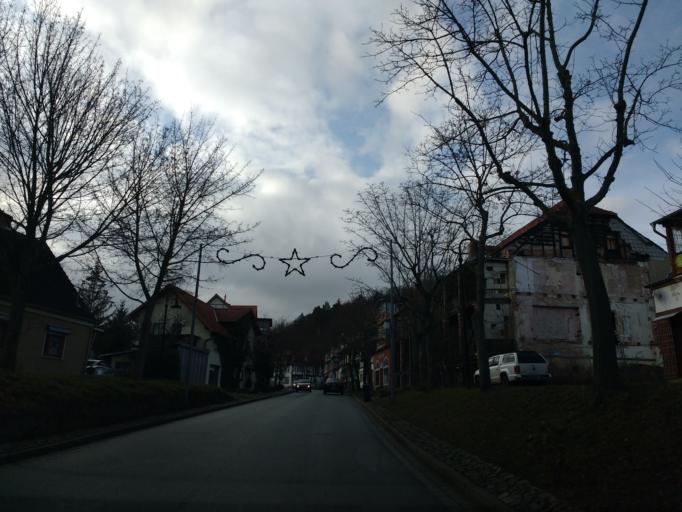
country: DE
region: Saxony-Anhalt
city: Bad Suderode
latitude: 51.7274
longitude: 11.1181
